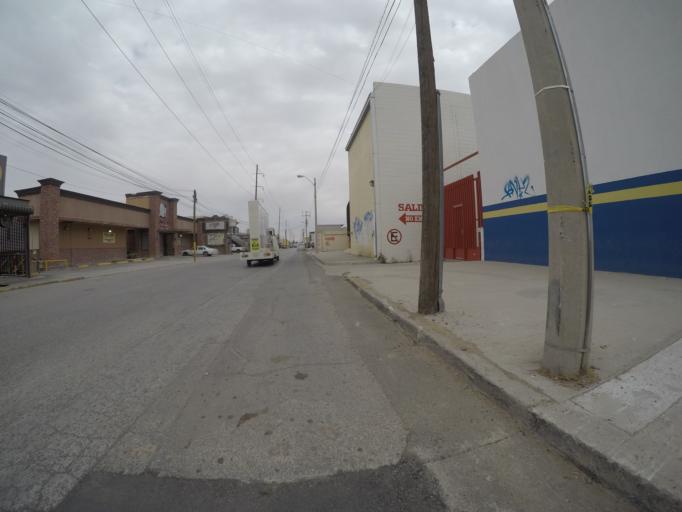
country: MX
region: Chihuahua
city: Ciudad Juarez
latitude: 31.7400
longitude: -106.4298
